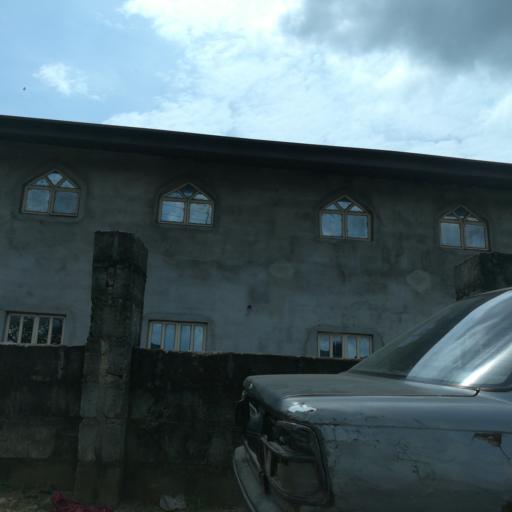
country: NG
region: Rivers
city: Port Harcourt
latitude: 4.7749
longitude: 7.0424
